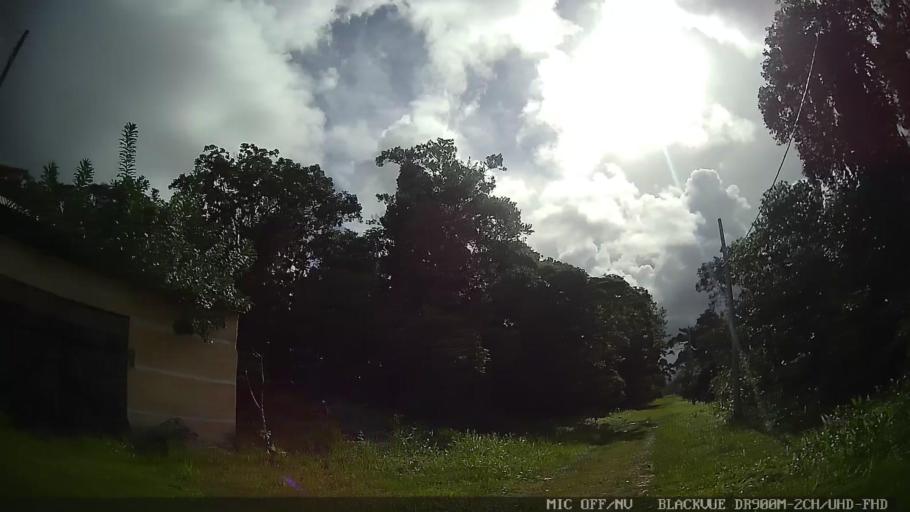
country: BR
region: Sao Paulo
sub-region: Itanhaem
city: Itanhaem
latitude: -24.2277
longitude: -46.8945
